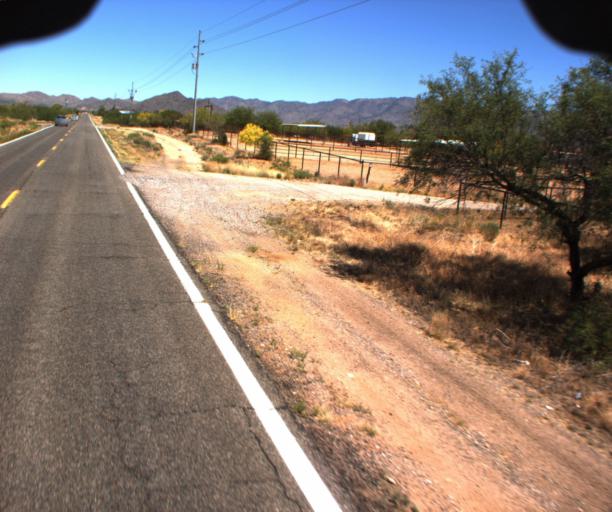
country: US
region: Arizona
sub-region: Yavapai County
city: Congress
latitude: 34.1389
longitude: -112.8411
